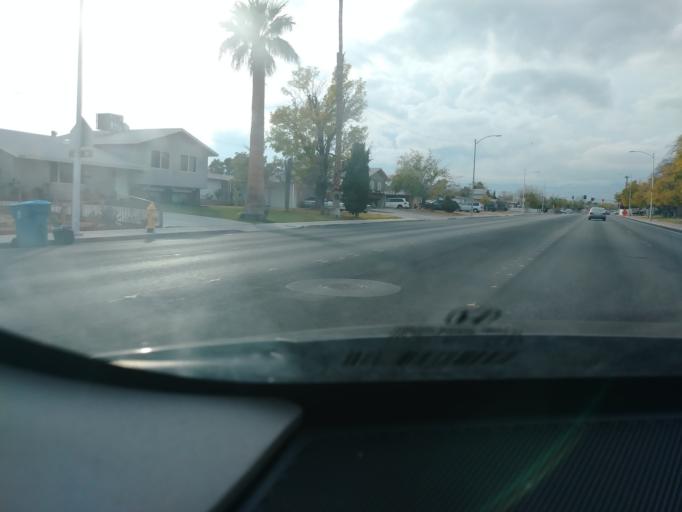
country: US
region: Nevada
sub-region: Clark County
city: Spring Valley
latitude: 36.1809
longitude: -115.2211
